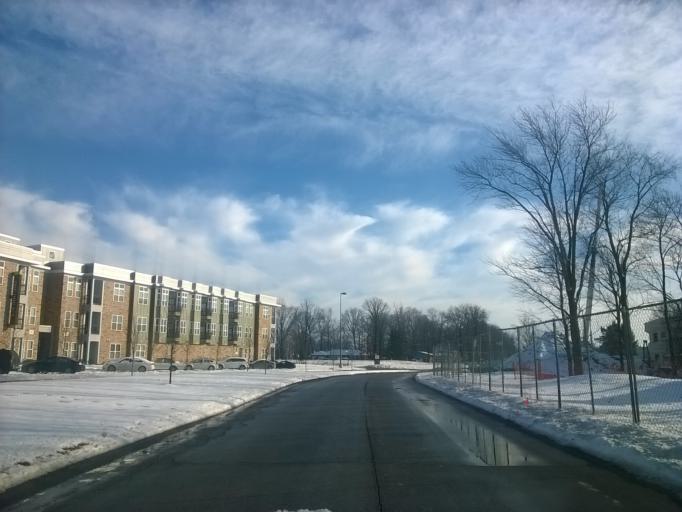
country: US
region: Indiana
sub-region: Hamilton County
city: Carmel
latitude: 39.9584
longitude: -86.1460
